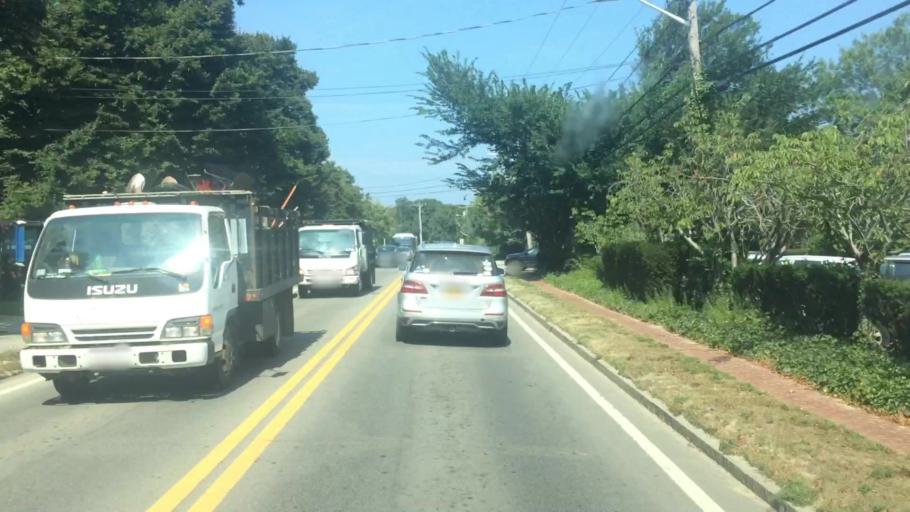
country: US
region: Massachusetts
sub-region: Dukes County
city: Edgartown
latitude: 41.3933
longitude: -70.5254
